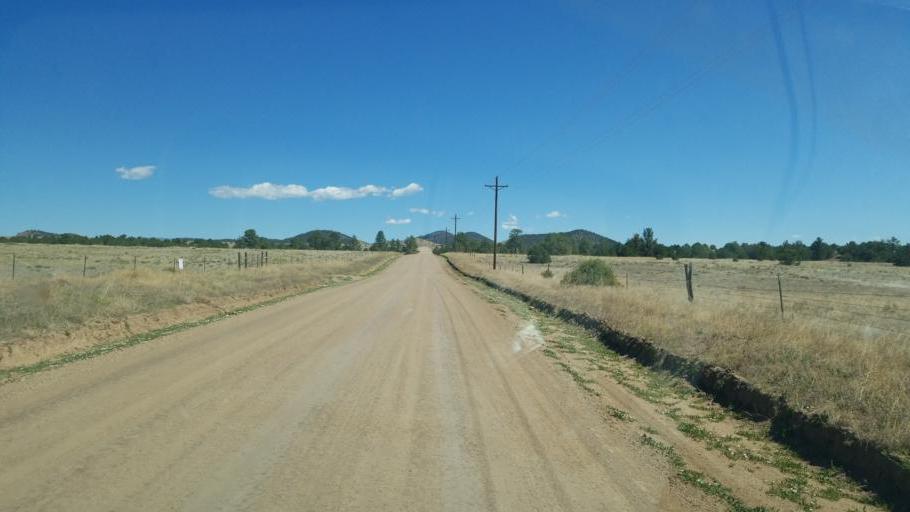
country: US
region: Colorado
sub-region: Custer County
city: Westcliffe
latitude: 38.2727
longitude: -105.5010
